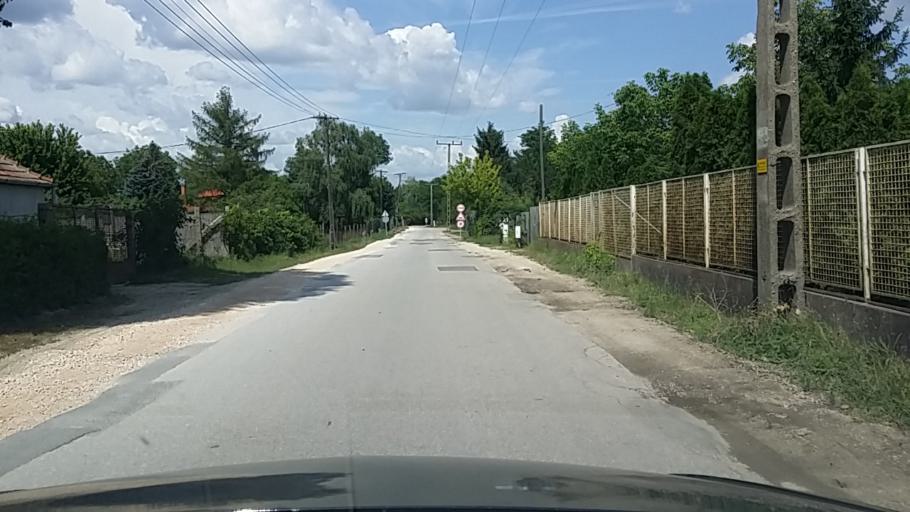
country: HU
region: Bacs-Kiskun
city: Kecskemet
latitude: 46.9253
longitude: 19.6588
